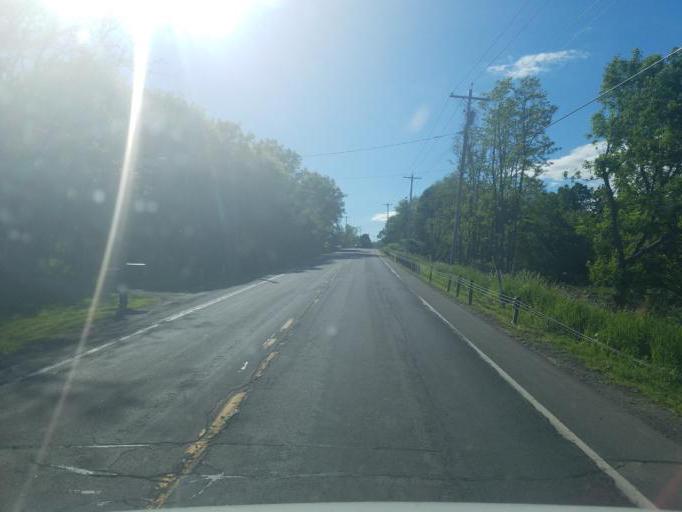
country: US
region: New York
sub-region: Herkimer County
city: Little Falls
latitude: 43.0054
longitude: -74.7826
